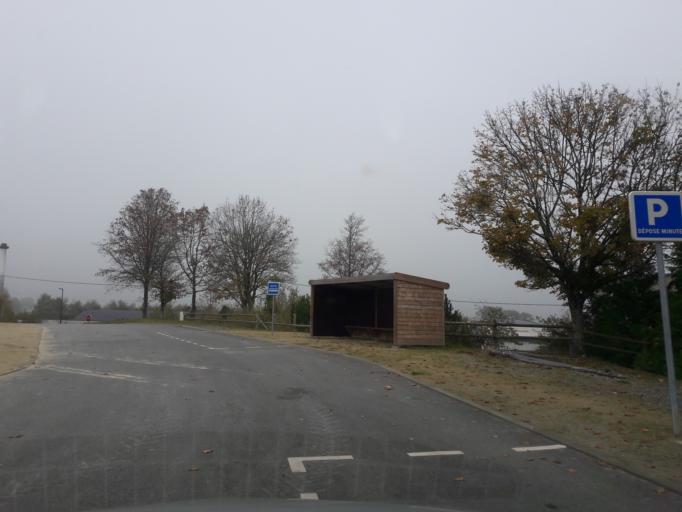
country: FR
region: Brittany
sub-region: Departement d'Ille-et-Vilaine
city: Janze
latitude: 47.9632
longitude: -1.4961
